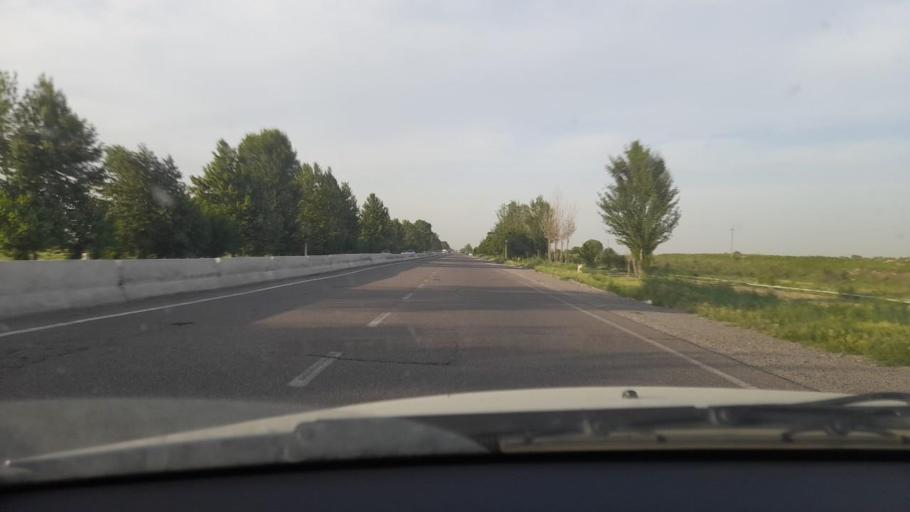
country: KZ
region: Ongtustik Qazaqstan
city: Myrzakent
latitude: 40.5483
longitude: 68.3587
